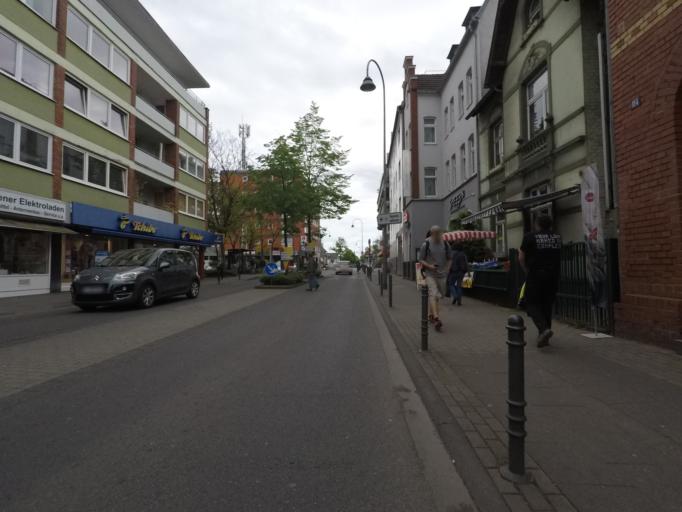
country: DE
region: North Rhine-Westphalia
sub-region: Regierungsbezirk Koln
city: Poll
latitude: 50.8924
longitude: 6.9959
